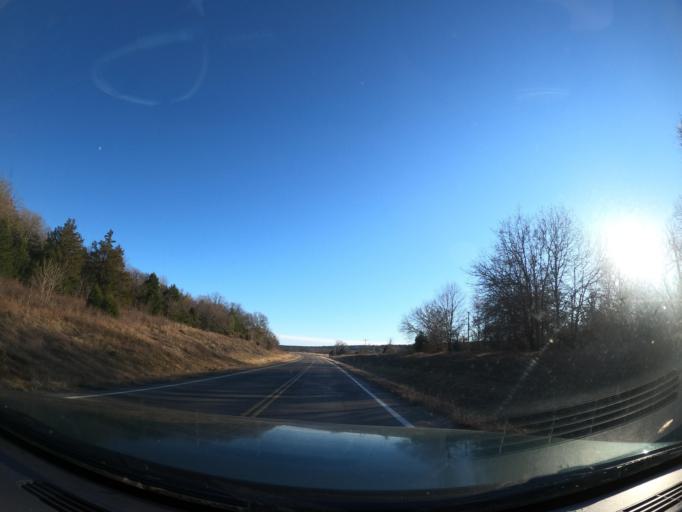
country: US
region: Oklahoma
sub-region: Latimer County
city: Wilburton
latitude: 34.9369
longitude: -95.3409
